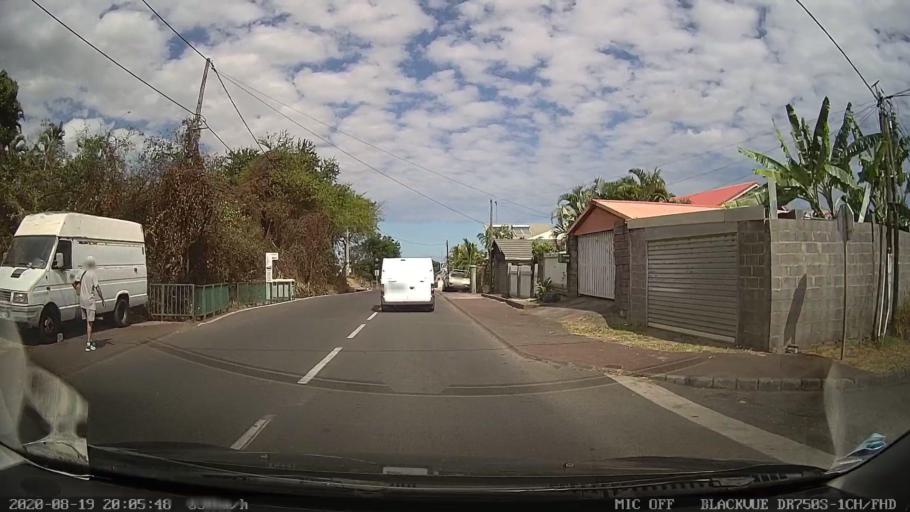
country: RE
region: Reunion
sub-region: Reunion
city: La Possession
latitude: -20.9550
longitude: 55.3381
